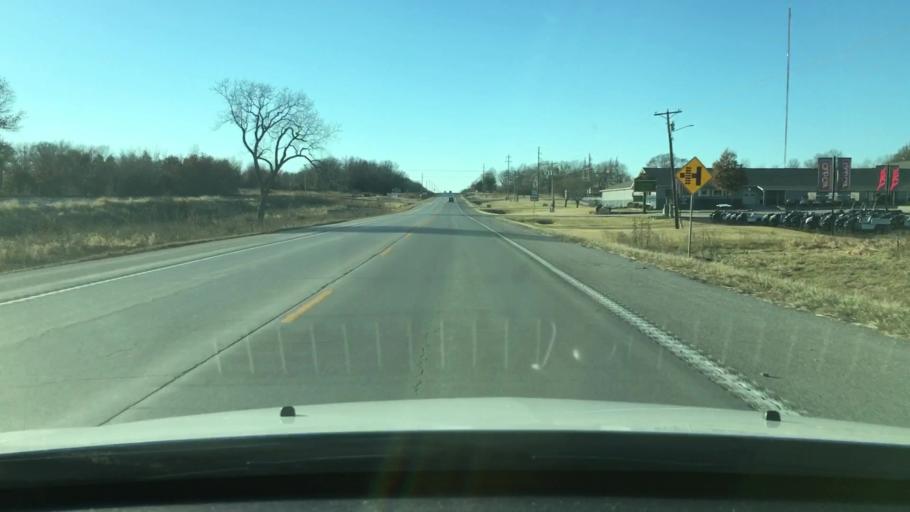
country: US
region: Missouri
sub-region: Audrain County
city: Mexico
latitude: 39.1856
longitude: -91.9345
